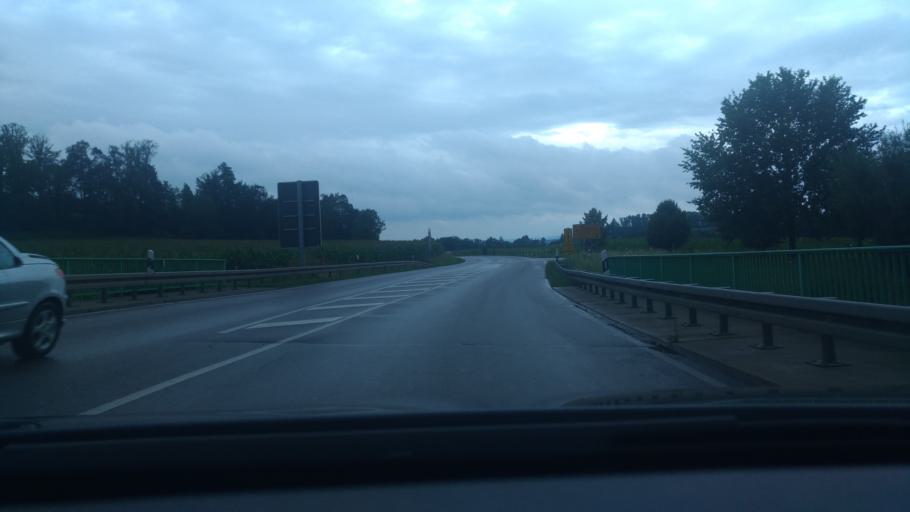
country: DE
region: Baden-Wuerttemberg
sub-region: Tuebingen Region
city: Owingen
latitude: 47.7922
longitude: 9.1474
